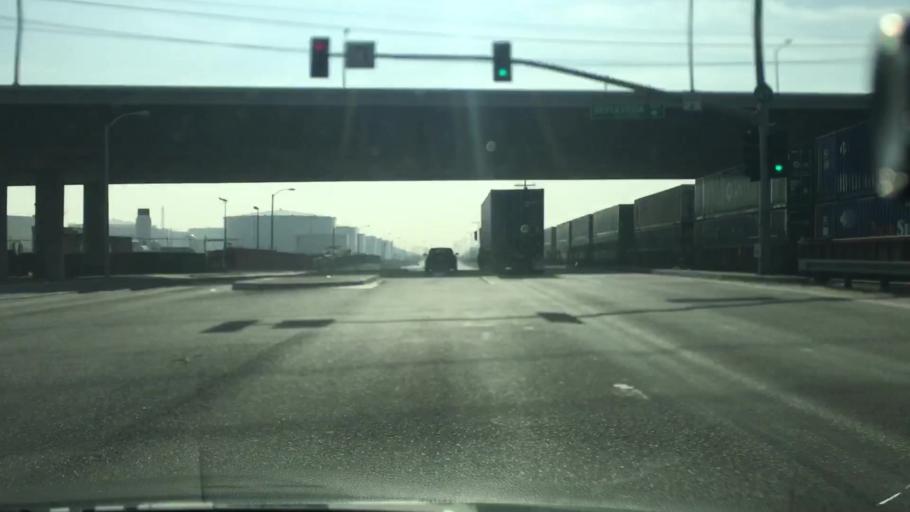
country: US
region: California
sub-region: Los Angeles County
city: Carson
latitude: 33.8083
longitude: -118.2347
